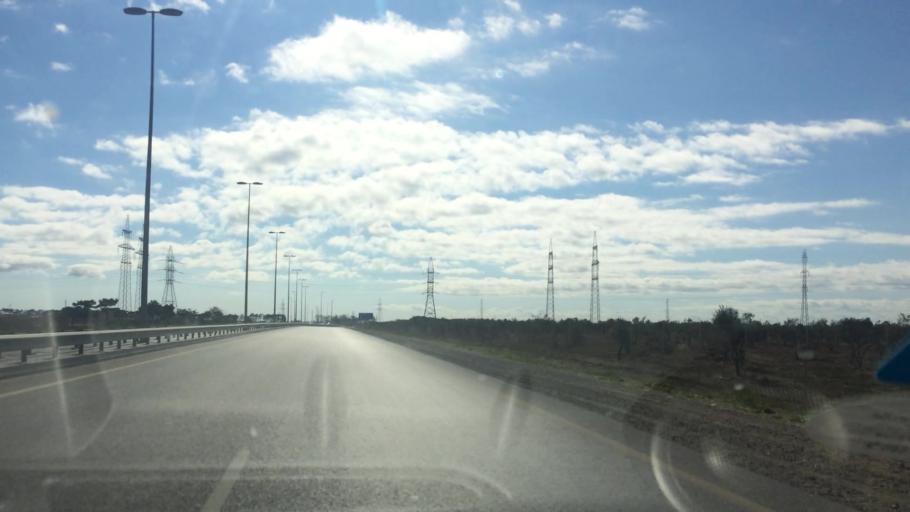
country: AZ
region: Baki
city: Qala
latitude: 40.4393
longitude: 50.1822
